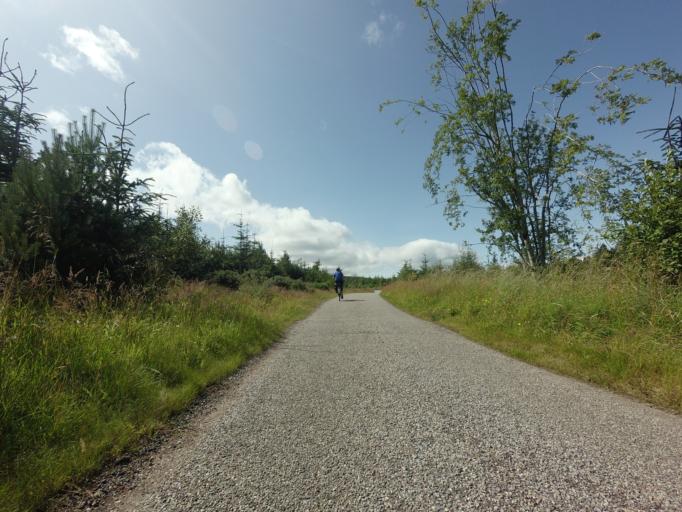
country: GB
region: Scotland
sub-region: Highland
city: Nairn
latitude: 57.4966
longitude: -3.9629
